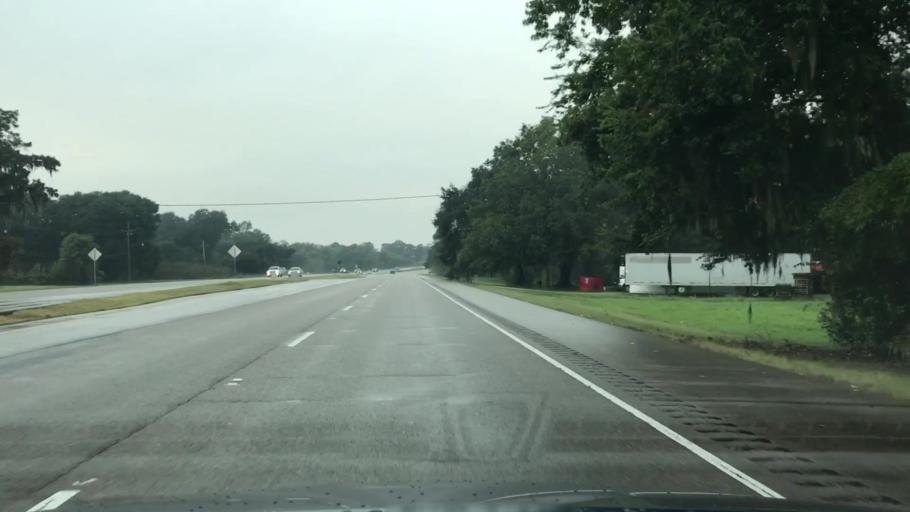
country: US
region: Louisiana
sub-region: Saint Charles Parish
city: Des Allemands
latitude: 29.8235
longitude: -90.4686
